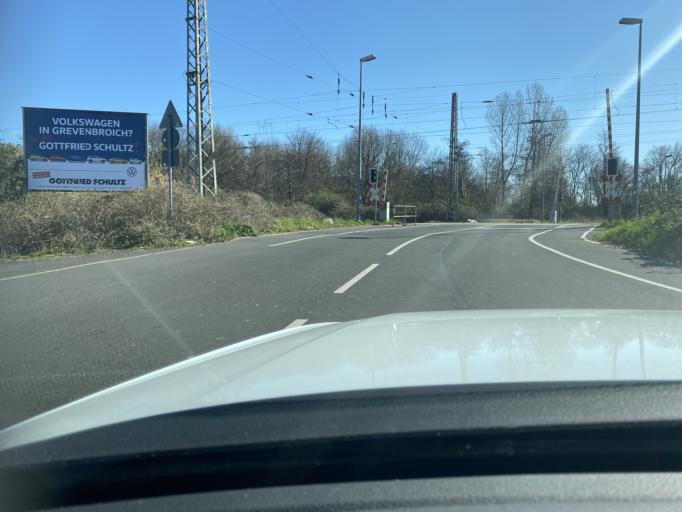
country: DE
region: North Rhine-Westphalia
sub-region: Regierungsbezirk Dusseldorf
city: Grevenbroich
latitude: 51.0984
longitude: 6.5820
